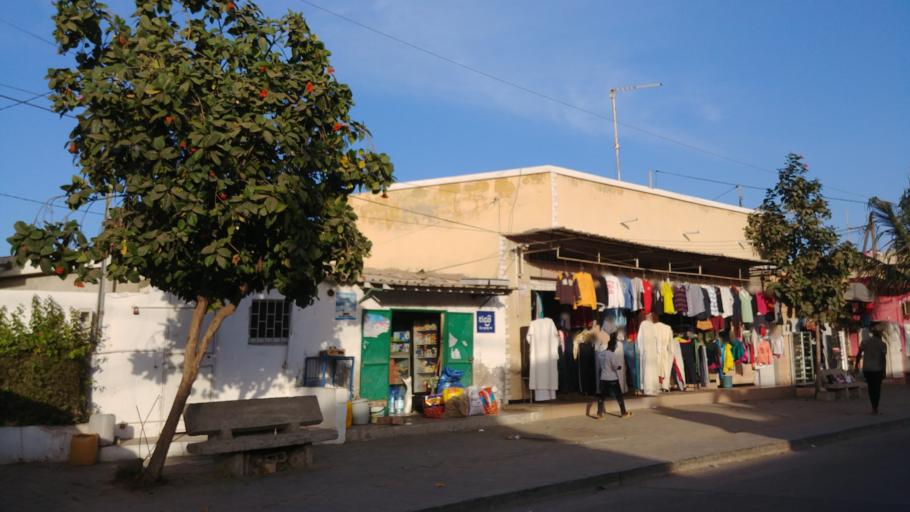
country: SN
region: Saint-Louis
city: Saint-Louis
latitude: 16.0239
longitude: -16.4938
